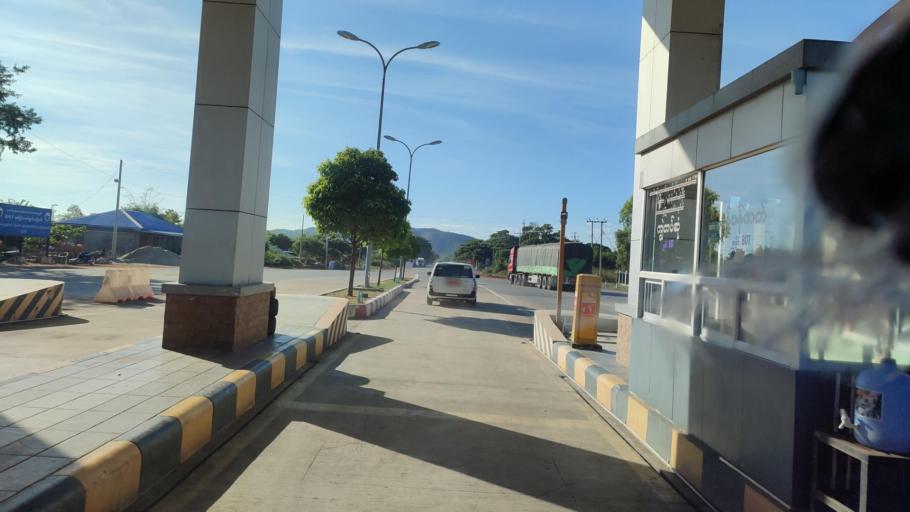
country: MM
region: Mandalay
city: Yamethin
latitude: 20.7527
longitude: 96.2613
